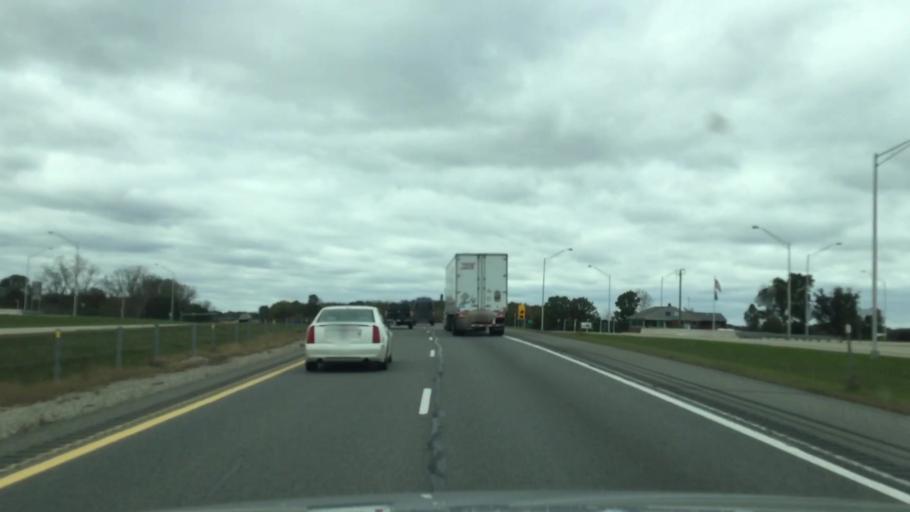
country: US
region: Michigan
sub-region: Jackson County
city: Grass Lake
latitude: 42.2937
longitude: -84.1765
